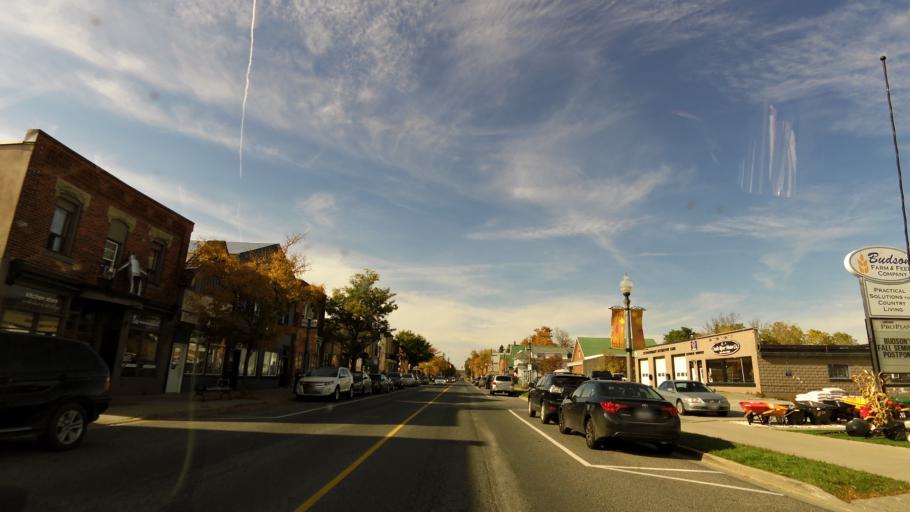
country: CA
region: Ontario
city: Orangeville
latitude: 43.7696
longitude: -80.0630
